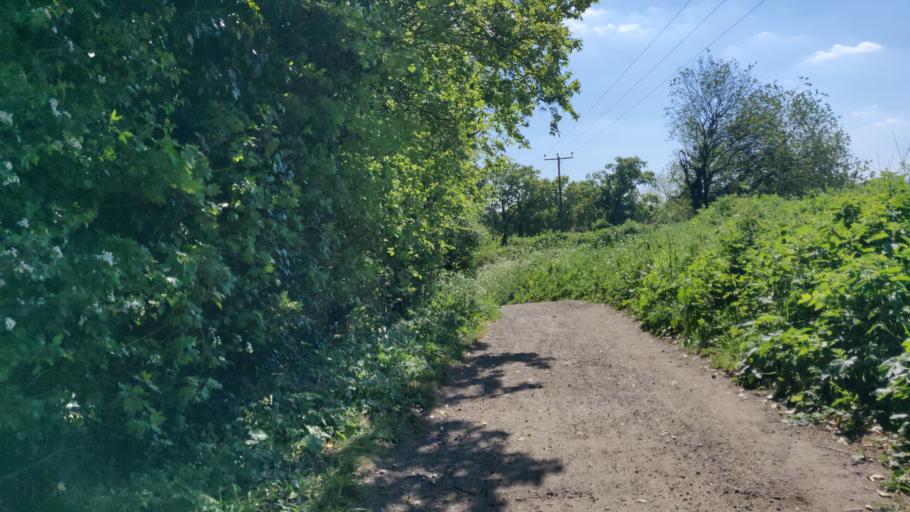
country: GB
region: England
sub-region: West Sussex
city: Southwater
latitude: 51.0552
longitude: -0.3755
